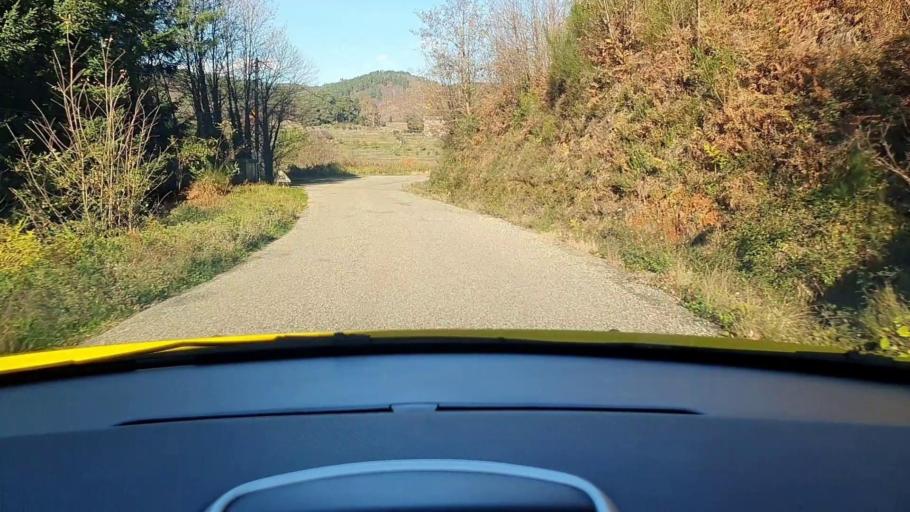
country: FR
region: Languedoc-Roussillon
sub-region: Departement du Gard
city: Branoux-les-Taillades
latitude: 44.2646
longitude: 3.9719
